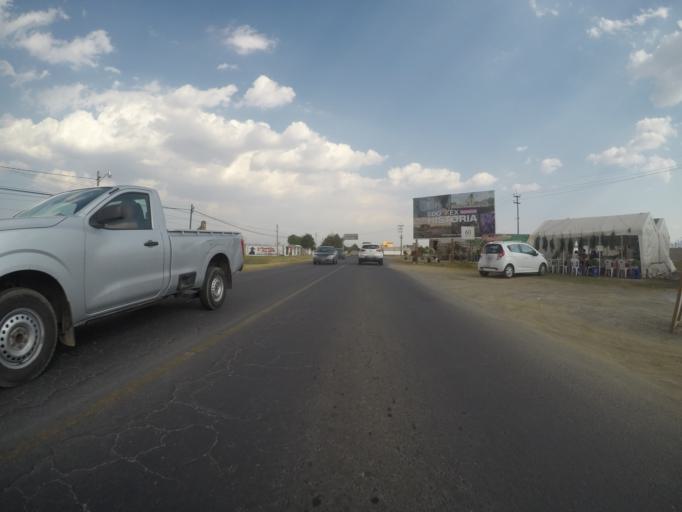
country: MX
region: Morelos
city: Chapultepec
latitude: 19.2010
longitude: -99.5481
